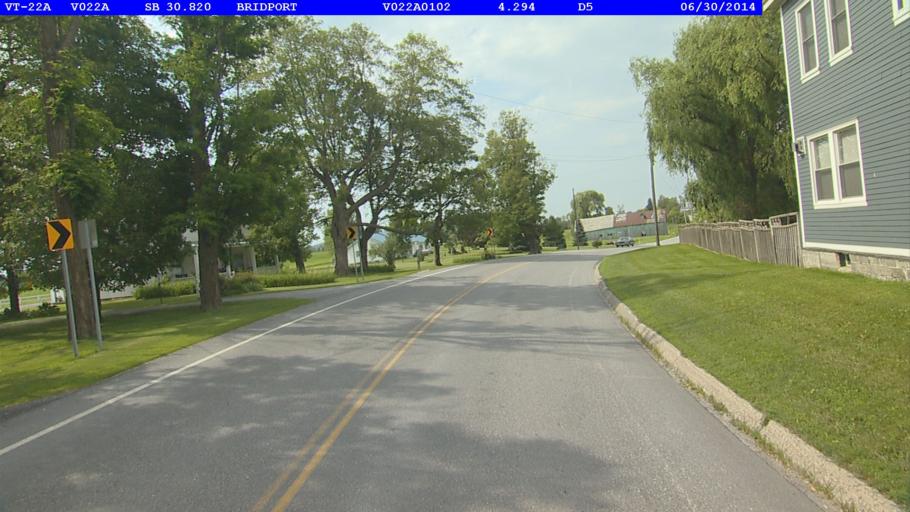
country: US
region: Vermont
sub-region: Addison County
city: Middlebury (village)
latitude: 44.0015
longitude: -73.3078
